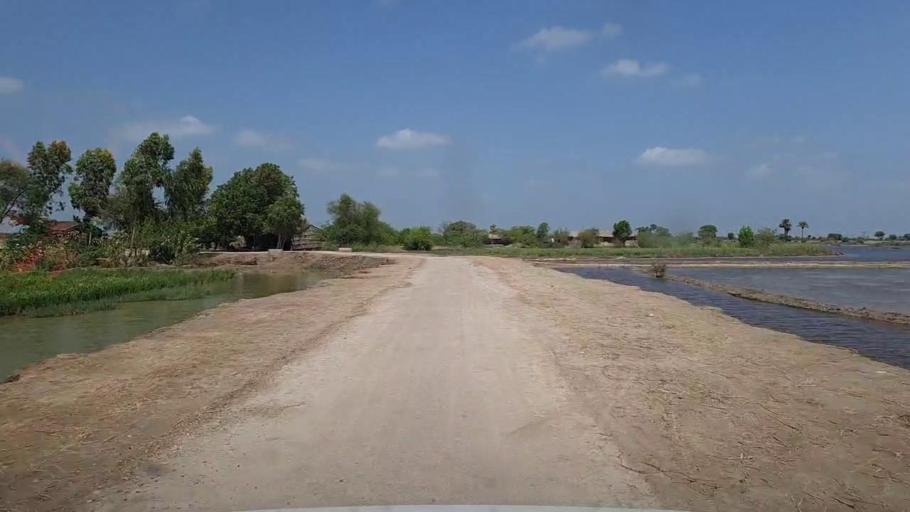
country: PK
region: Sindh
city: Kario
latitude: 24.6930
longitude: 68.5880
